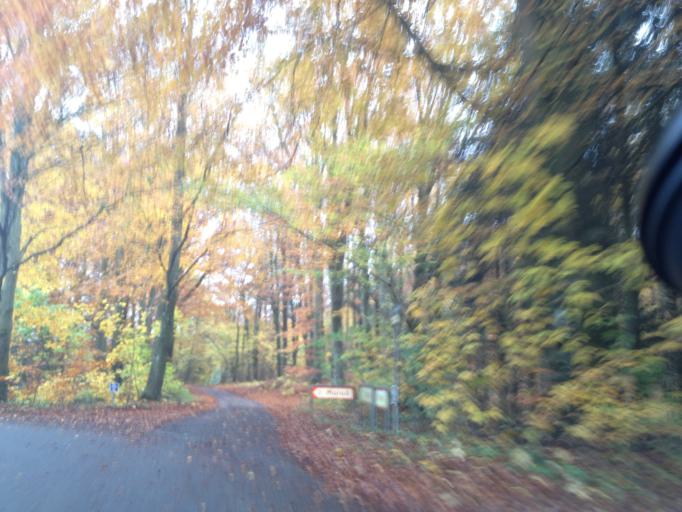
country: DK
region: South Denmark
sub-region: Assens Kommune
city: Vissenbjerg
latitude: 55.4341
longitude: 10.1697
